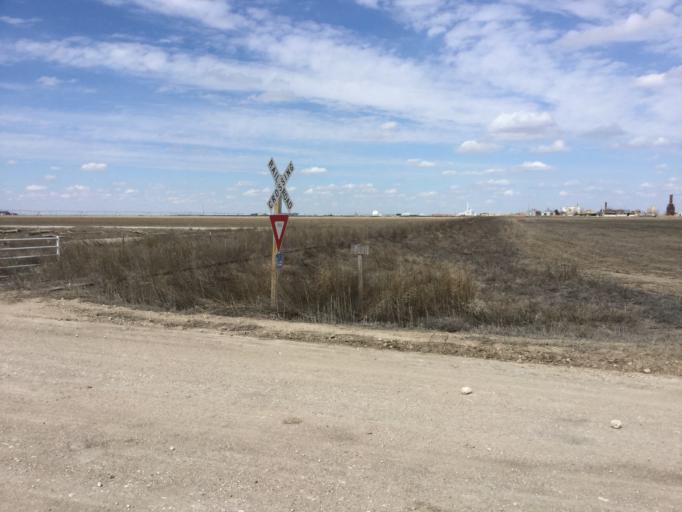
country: US
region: Kansas
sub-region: Scott County
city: Scott City
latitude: 38.3085
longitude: -100.9143
